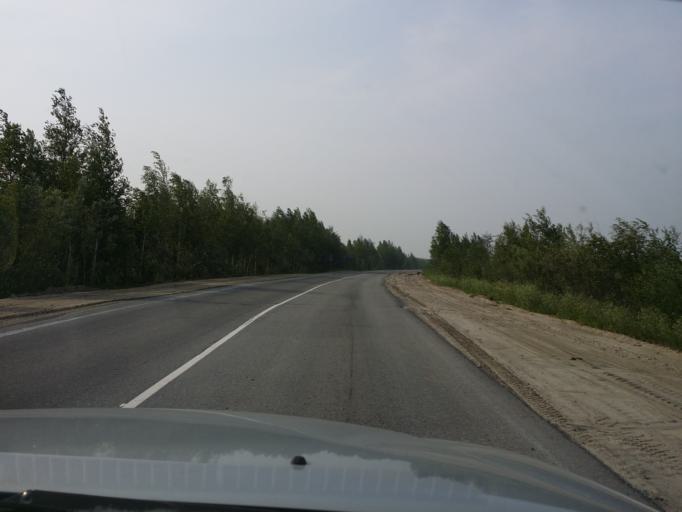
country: RU
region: Khanty-Mansiyskiy Avtonomnyy Okrug
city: Nizhnevartovsk
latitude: 61.1057
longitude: 76.6137
